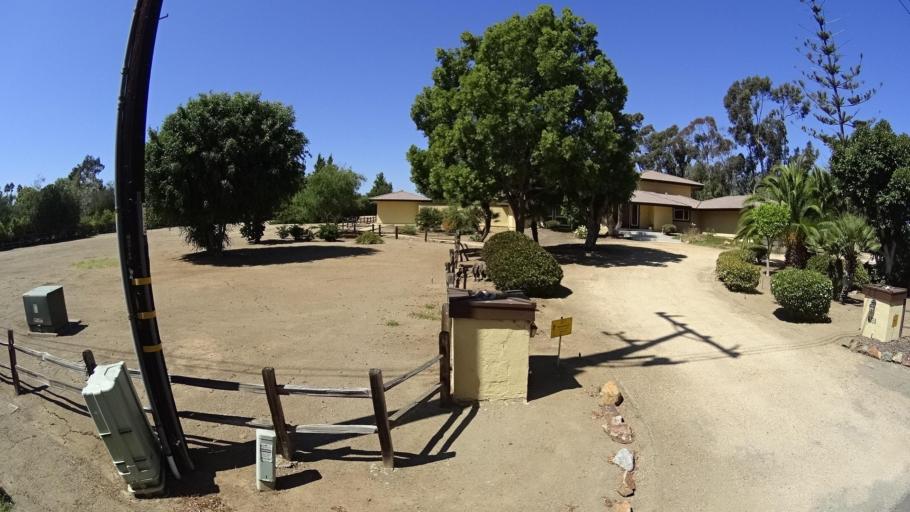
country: US
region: California
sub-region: San Diego County
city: Rancho Santa Fe
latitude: 33.0337
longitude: -117.1961
